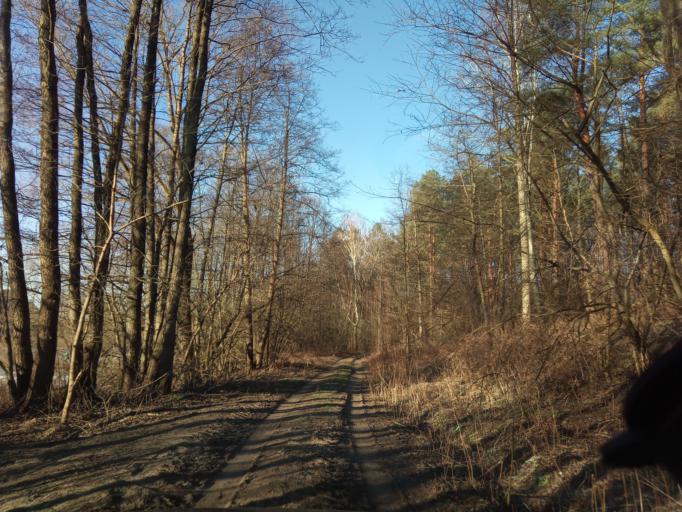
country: LT
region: Alytaus apskritis
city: Druskininkai
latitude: 53.9502
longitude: 23.8669
